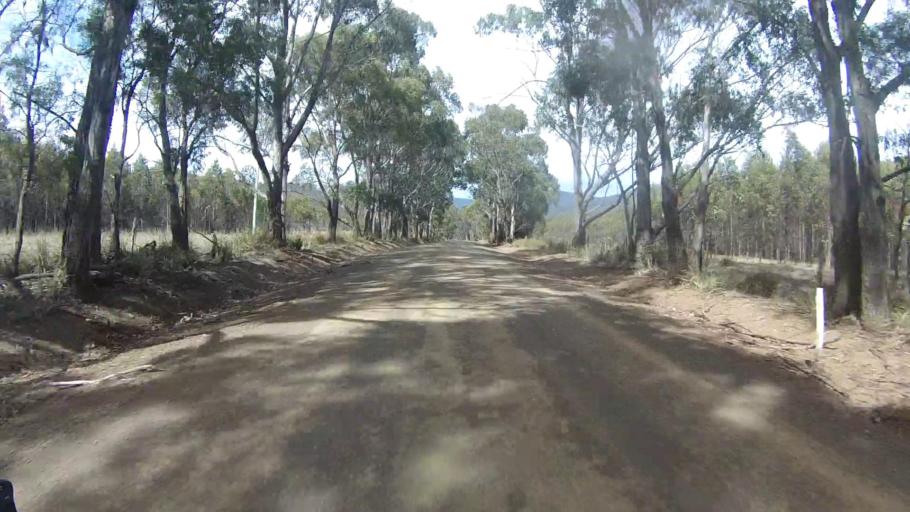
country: AU
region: Tasmania
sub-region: Sorell
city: Sorell
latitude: -42.6600
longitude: 147.8957
